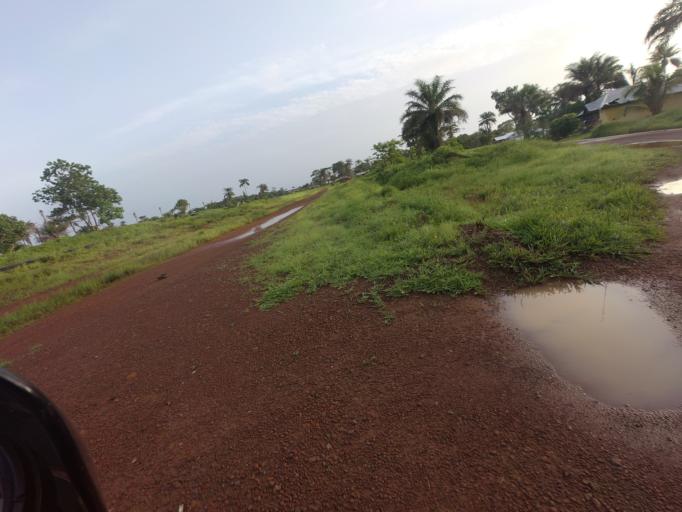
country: SL
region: Northern Province
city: Kambia
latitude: 9.0905
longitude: -12.9086
